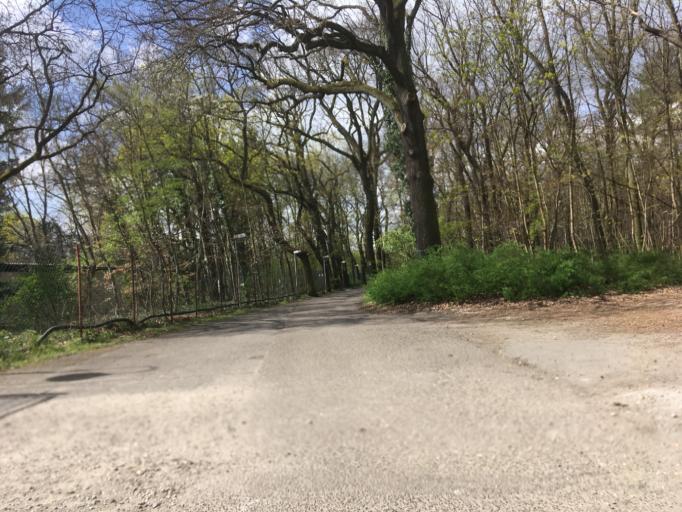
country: DE
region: Berlin
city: Kopenick Bezirk
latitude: 52.4575
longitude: 13.5661
